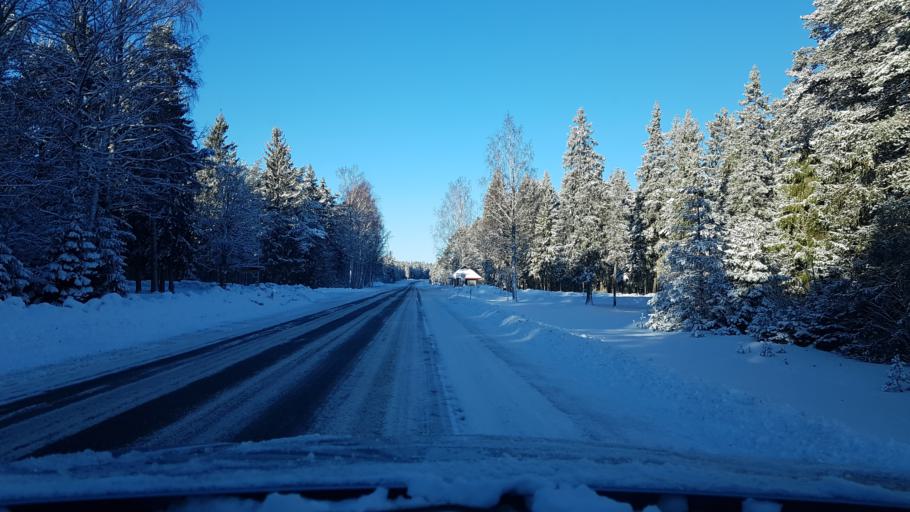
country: EE
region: Hiiumaa
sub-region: Kaerdla linn
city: Kardla
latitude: 58.9622
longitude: 22.8456
